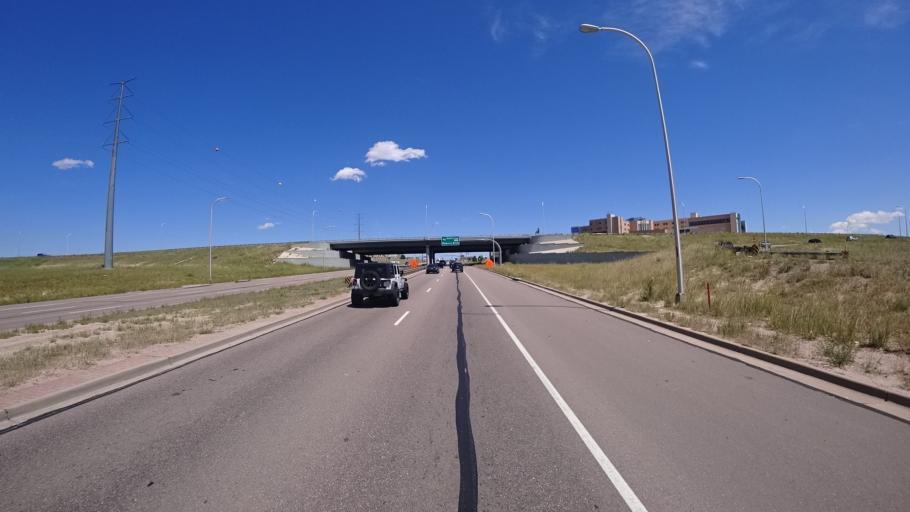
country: US
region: Colorado
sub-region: El Paso County
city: Black Forest
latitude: 38.9401
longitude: -104.7215
